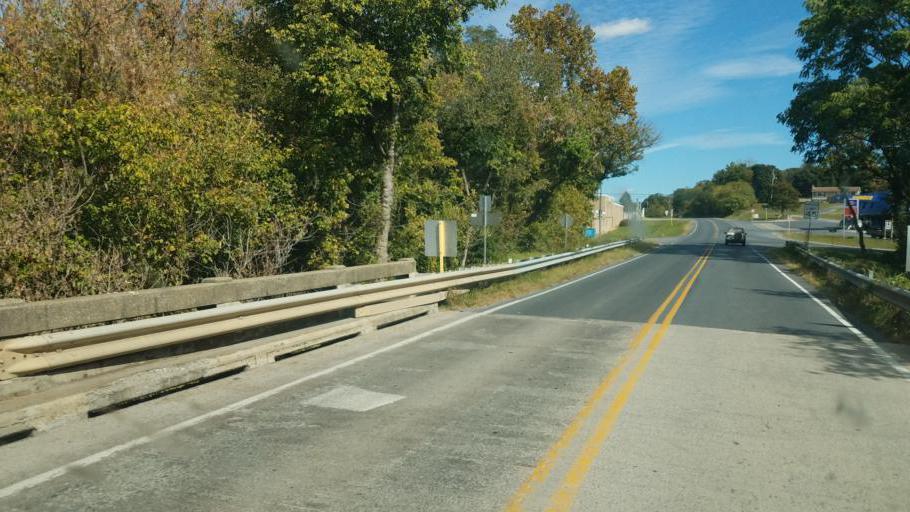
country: US
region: Virginia
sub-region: Page County
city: Stanley
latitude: 38.5889
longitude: -78.5648
